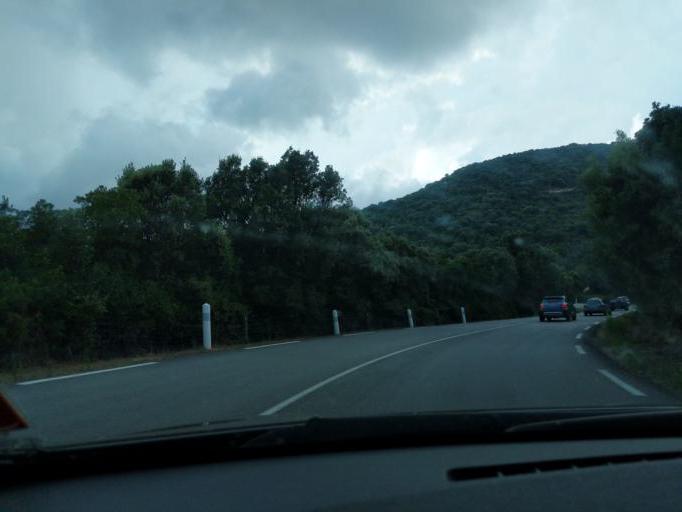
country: FR
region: Corsica
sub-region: Departement de la Corse-du-Sud
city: Sartene
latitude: 41.5794
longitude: 8.9485
